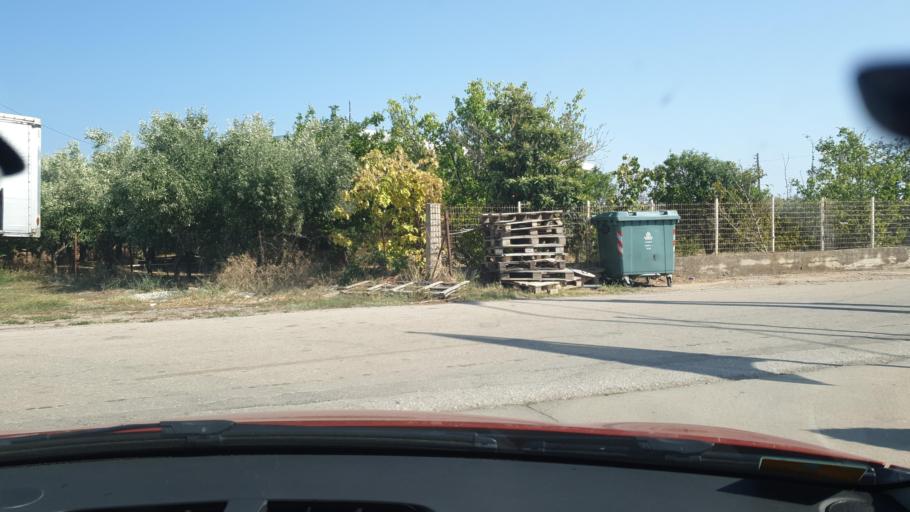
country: GR
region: Central Greece
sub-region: Nomos Fthiotidos
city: Livanates
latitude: 38.7183
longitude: 23.0495
